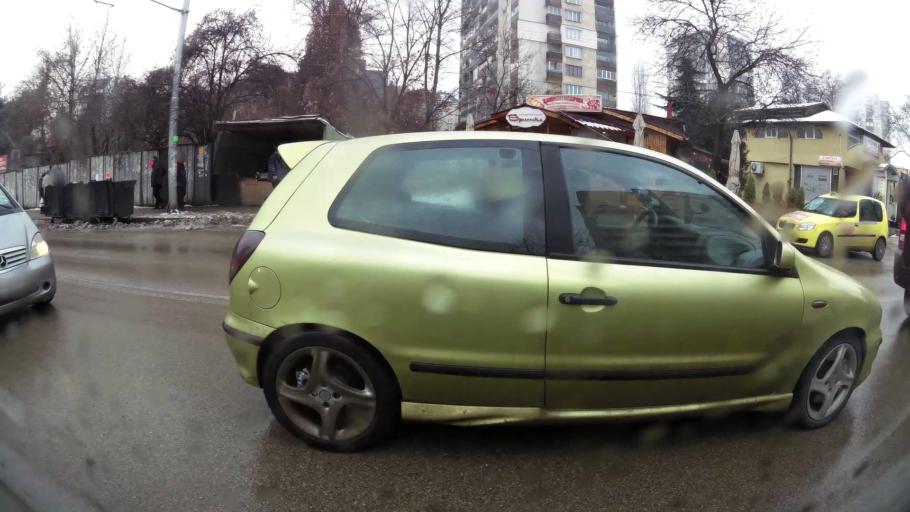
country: BG
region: Sofia-Capital
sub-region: Stolichna Obshtina
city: Sofia
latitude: 42.6692
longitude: 23.2777
